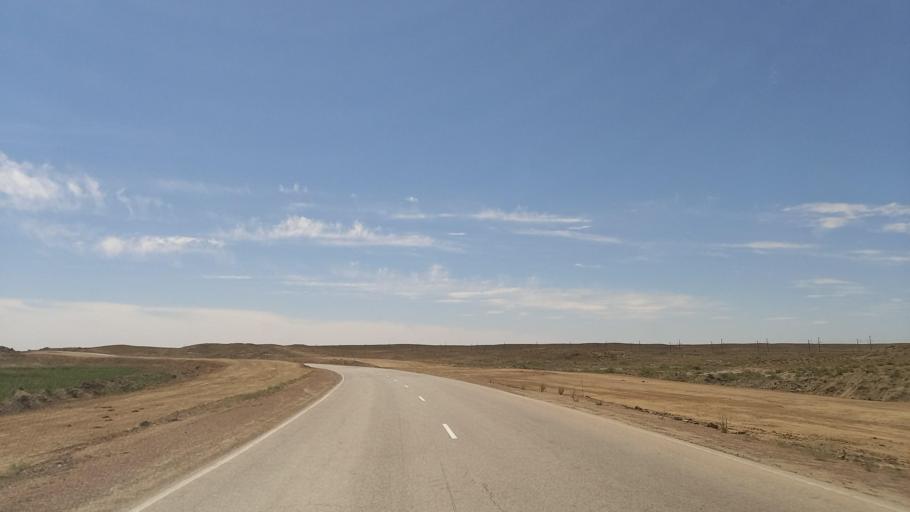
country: KZ
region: Almaty Oblysy
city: Ulken
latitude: 45.0024
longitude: 73.9958
